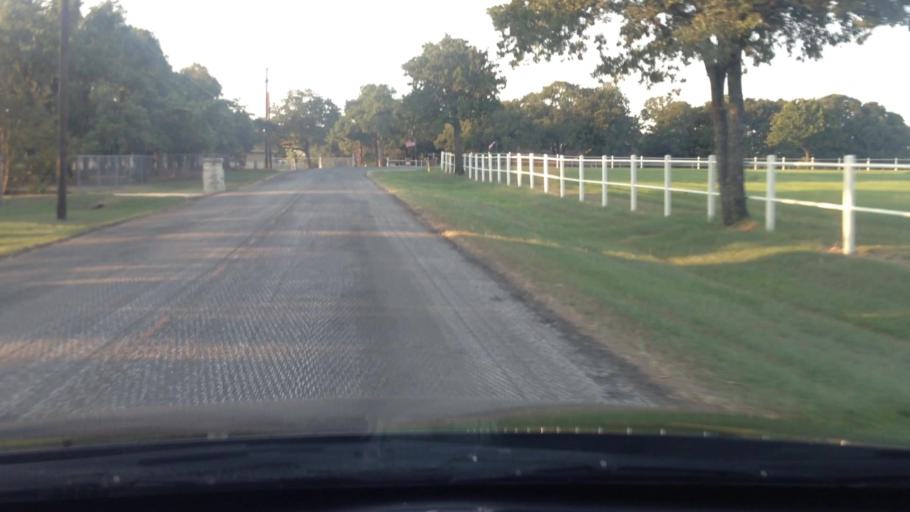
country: US
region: Texas
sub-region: Tarrant County
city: Rendon
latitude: 32.6008
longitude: -97.2405
